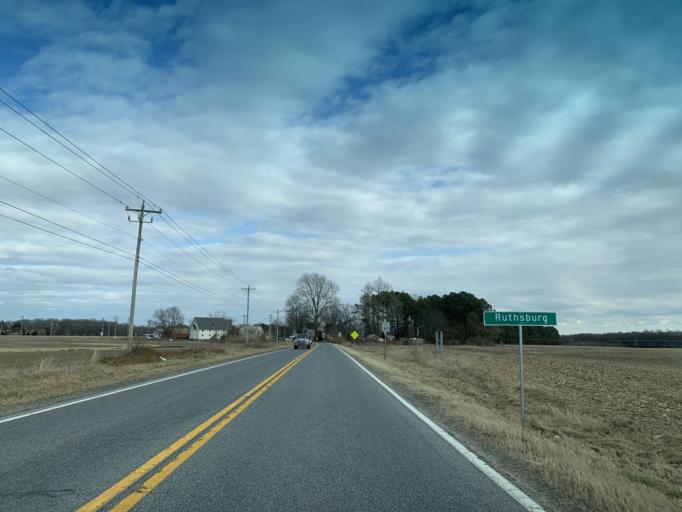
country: US
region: Maryland
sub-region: Caroline County
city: Ridgely
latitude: 39.0044
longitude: -75.9621
